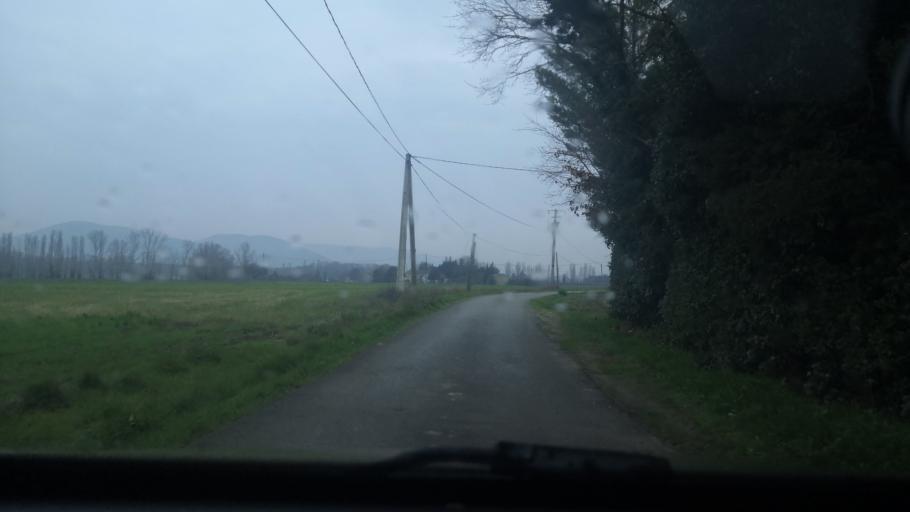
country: FR
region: Rhone-Alpes
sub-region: Departement de la Drome
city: Saint-Marcel-les-Sauzet
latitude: 44.5808
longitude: 4.8106
